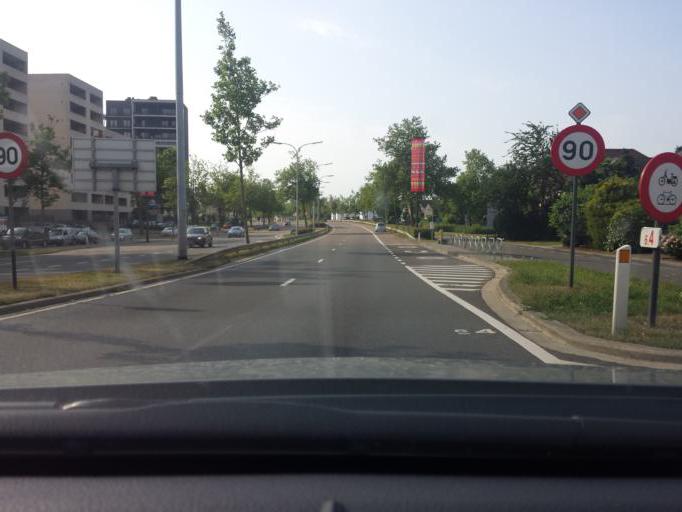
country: BE
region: Flanders
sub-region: Provincie Limburg
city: Hasselt
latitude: 50.9240
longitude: 5.3183
